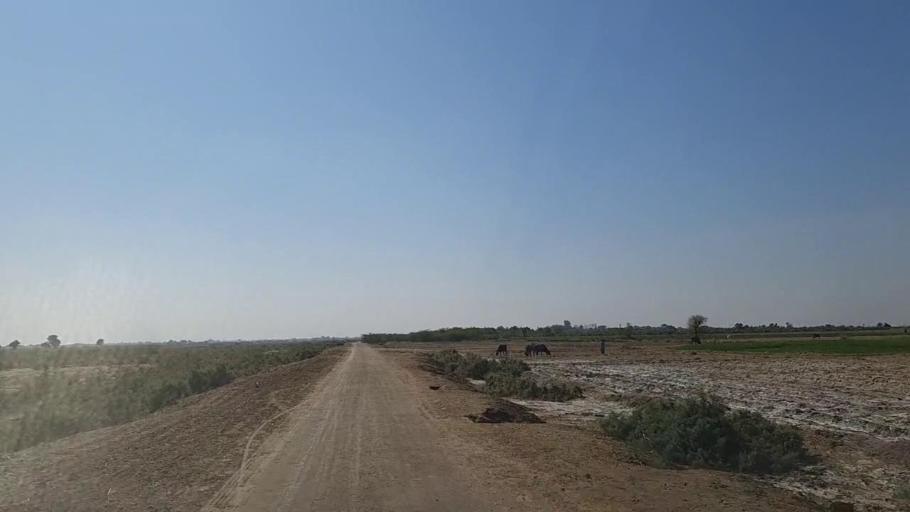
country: PK
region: Sindh
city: Pithoro
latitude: 25.4249
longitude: 69.3767
